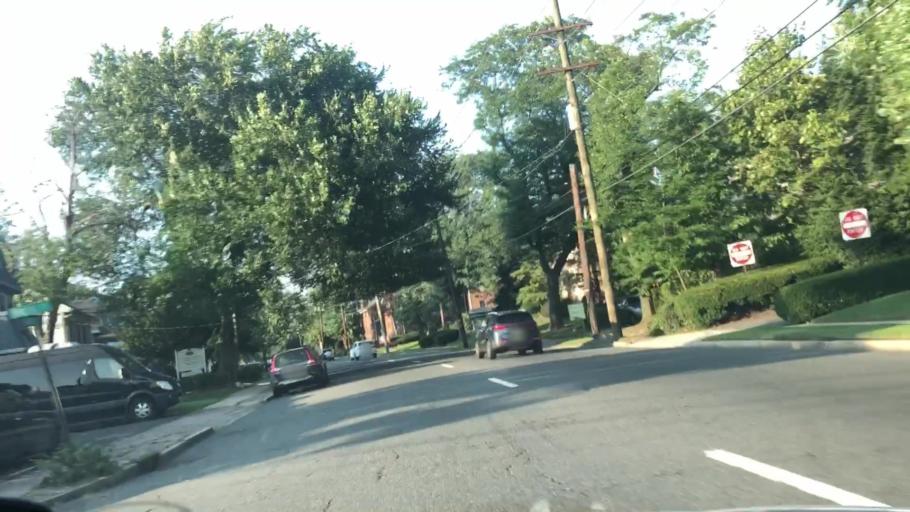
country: US
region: New Jersey
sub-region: Bergen County
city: Englewood
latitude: 40.8815
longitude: -73.9784
